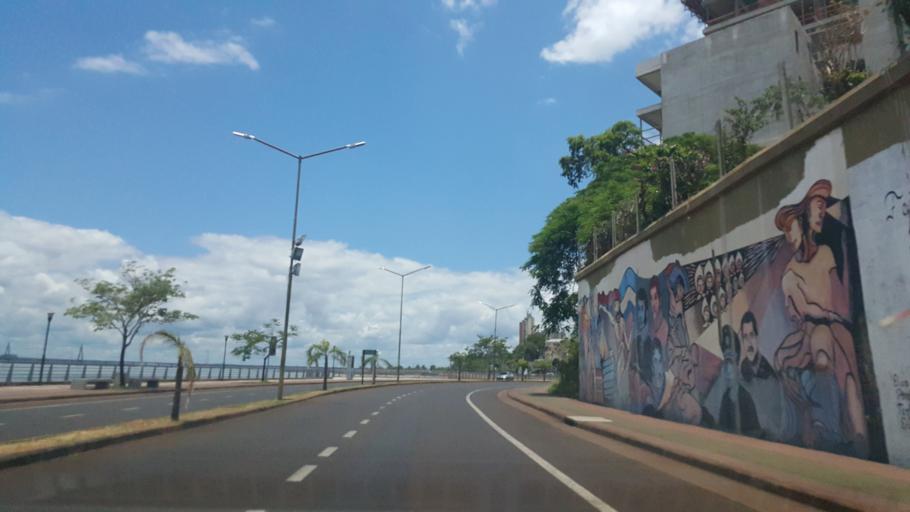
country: AR
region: Misiones
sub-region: Departamento de Capital
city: Posadas
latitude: -27.3561
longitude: -55.8914
